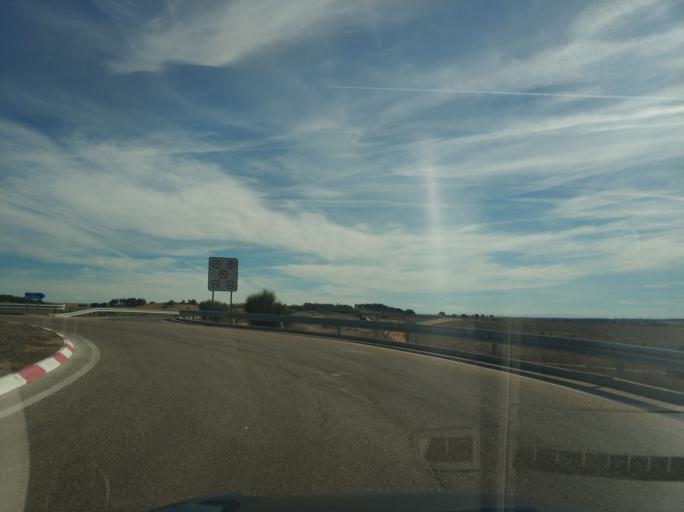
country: ES
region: Castille and Leon
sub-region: Provincia de Zamora
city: Cuelgamures
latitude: 41.2632
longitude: -5.7051
